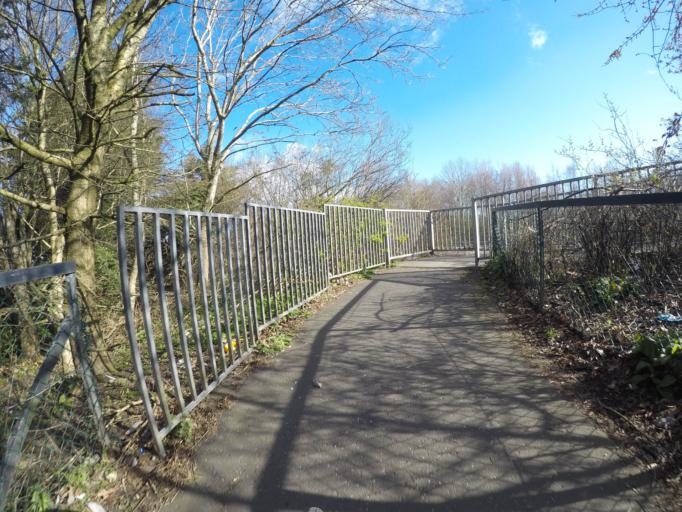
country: GB
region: Scotland
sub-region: North Ayrshire
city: Irvine
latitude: 55.6273
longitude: -4.6550
